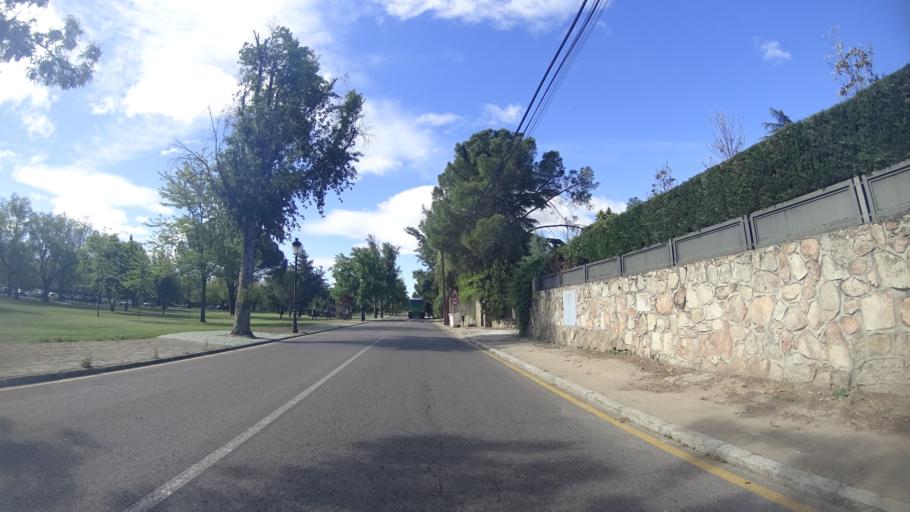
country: ES
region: Madrid
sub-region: Provincia de Madrid
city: Villanueva del Pardillo
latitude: 40.4736
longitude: -3.9424
